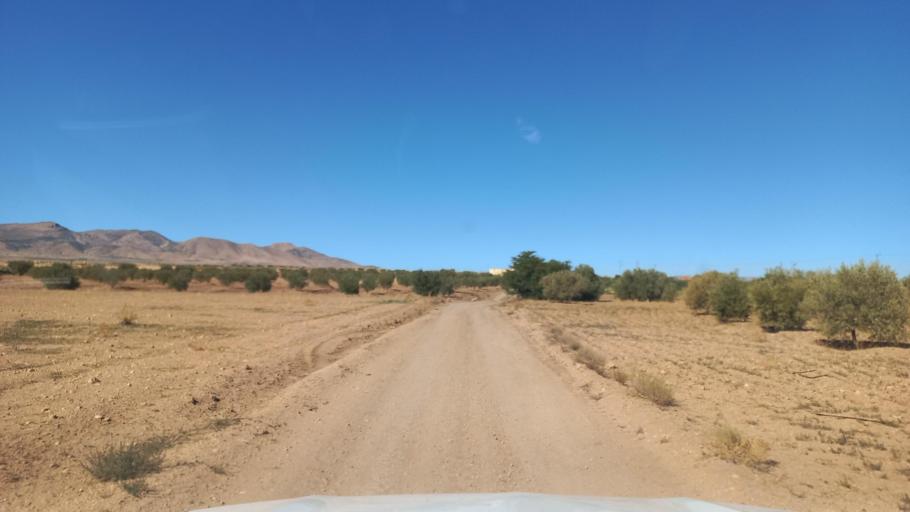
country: TN
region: Al Qasrayn
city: Sbiba
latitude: 35.3955
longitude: 9.0836
